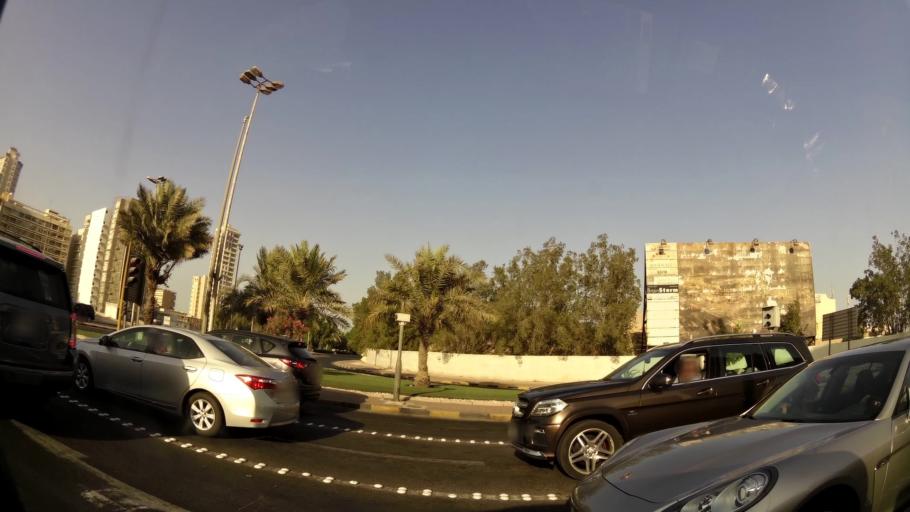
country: KW
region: Muhafazat Hawalli
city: As Salimiyah
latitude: 29.3460
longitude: 48.0955
